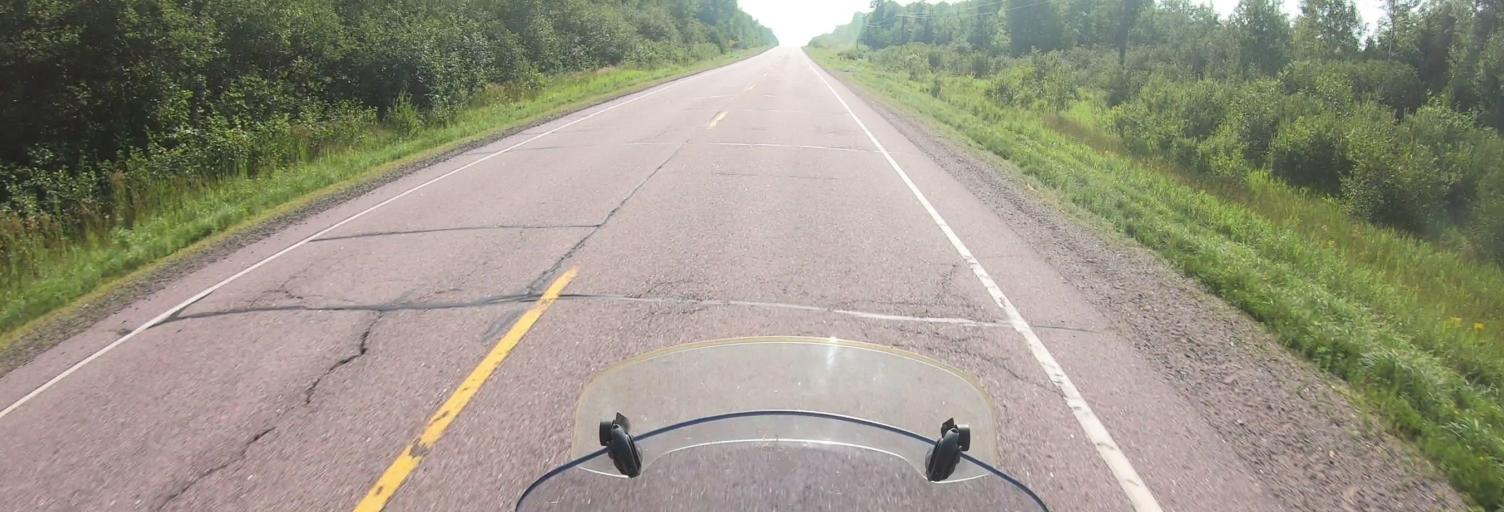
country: US
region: Wisconsin
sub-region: Iron County
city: Hurley
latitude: 46.3634
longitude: -90.4381
